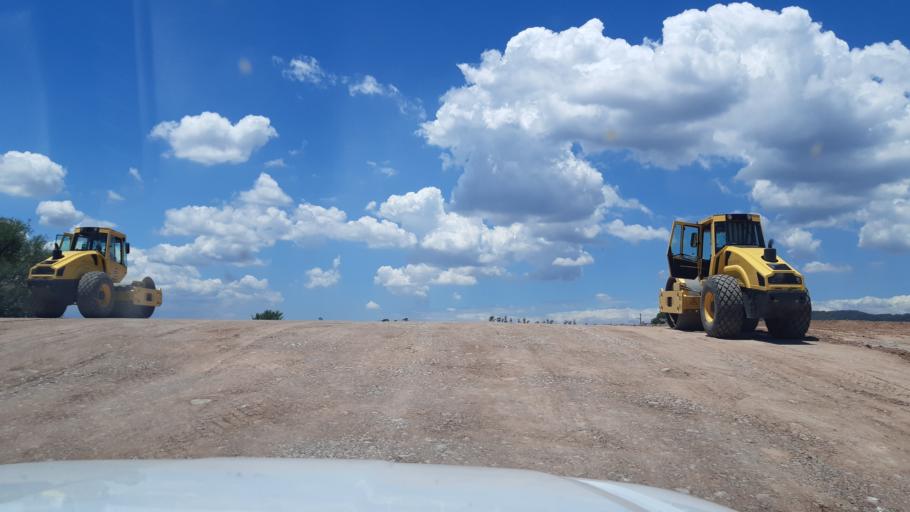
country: AR
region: Jujuy
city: La Mendieta
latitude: -24.4591
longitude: -65.0251
